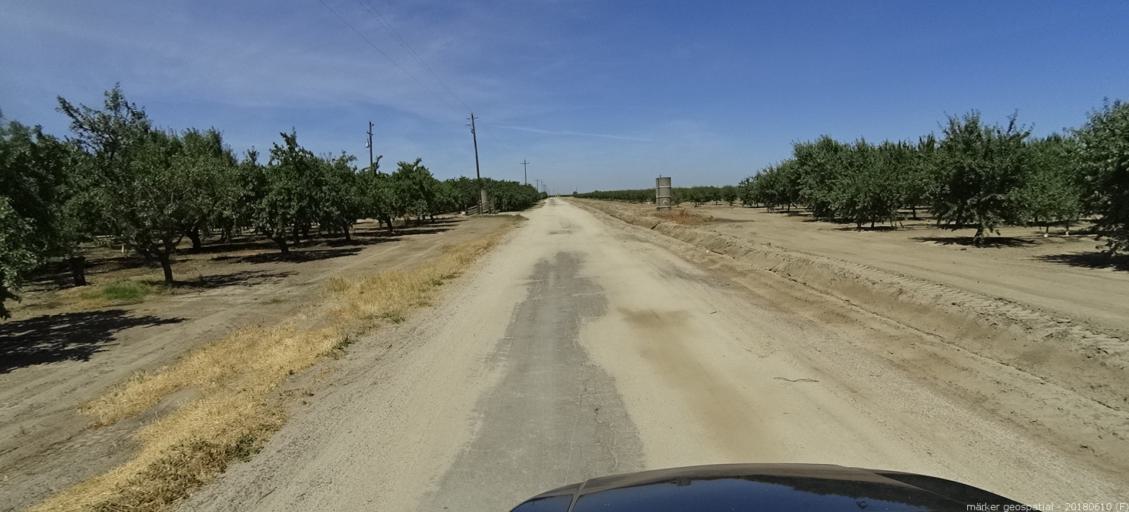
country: US
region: California
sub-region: Madera County
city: Chowchilla
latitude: 37.0399
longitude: -120.4141
